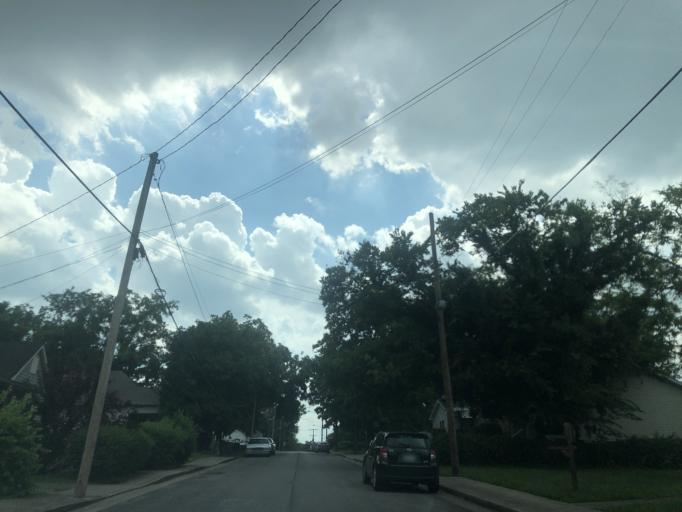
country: US
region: Tennessee
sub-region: Davidson County
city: Nashville
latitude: 36.1663
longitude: -86.8146
